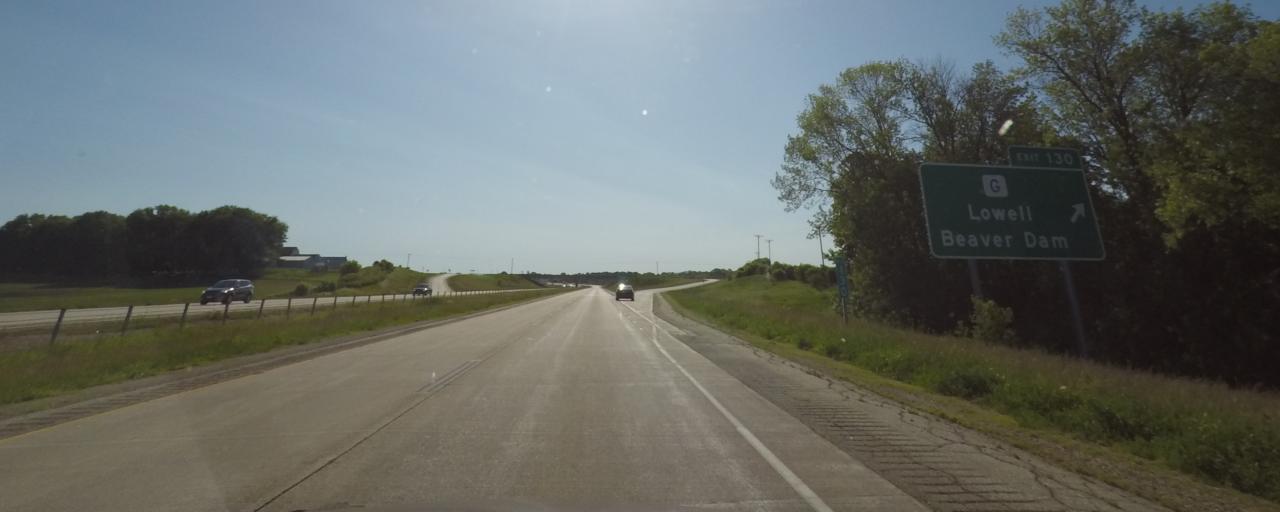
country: US
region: Wisconsin
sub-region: Dodge County
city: Beaver Dam
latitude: 43.4356
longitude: -88.8498
